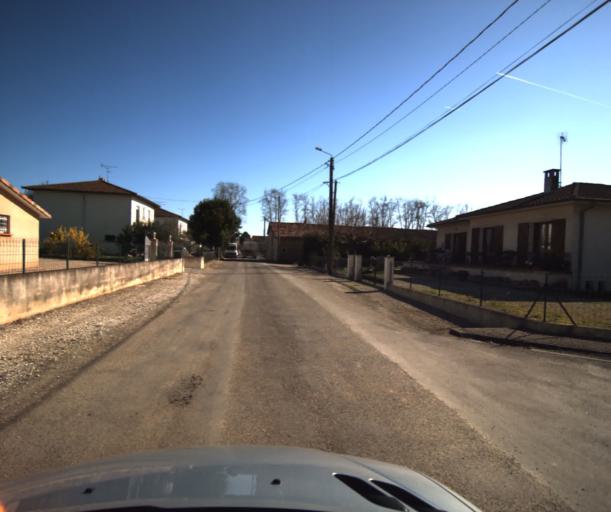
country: FR
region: Midi-Pyrenees
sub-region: Departement du Tarn-et-Garonne
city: Bressols
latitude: 43.9682
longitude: 1.3350
